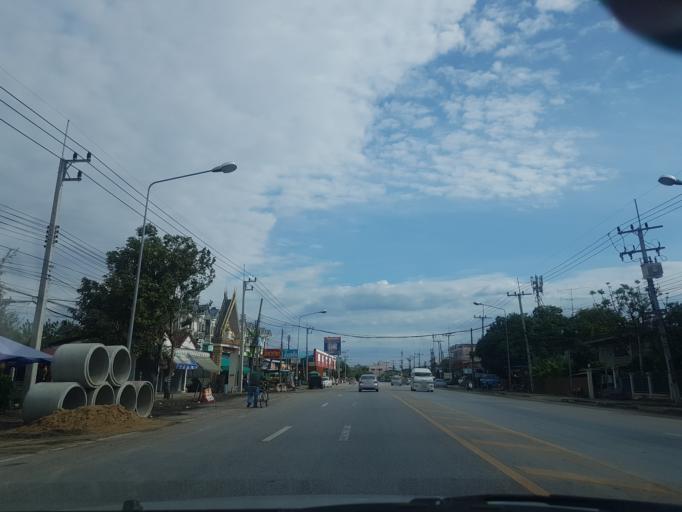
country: TH
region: Lop Buri
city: Lop Buri
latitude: 14.7882
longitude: 100.7006
